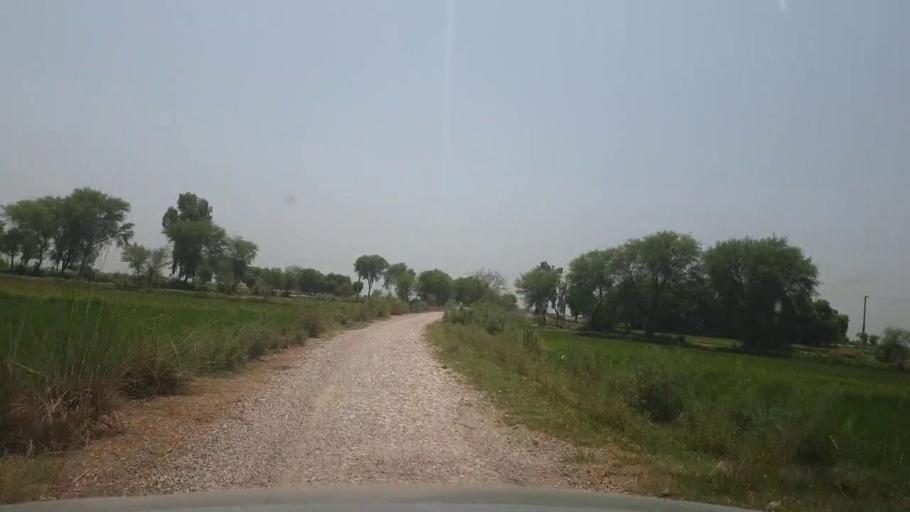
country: PK
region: Sindh
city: Lakhi
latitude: 27.8468
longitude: 68.6643
